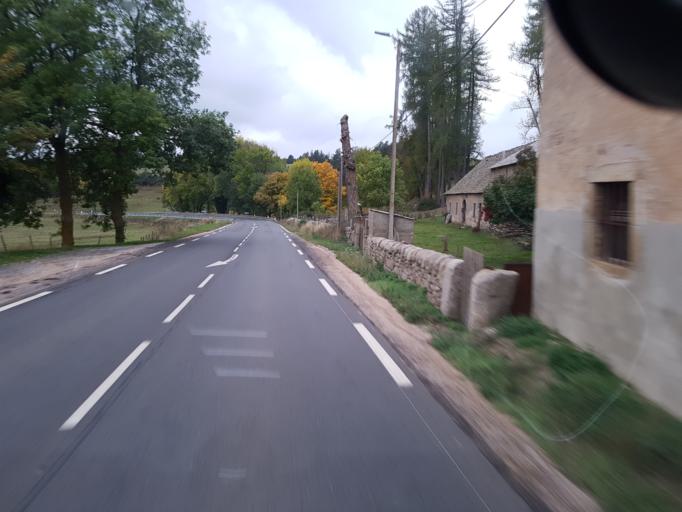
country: FR
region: Languedoc-Roussillon
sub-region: Departement de la Lozere
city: Mende
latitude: 44.5799
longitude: 3.6339
